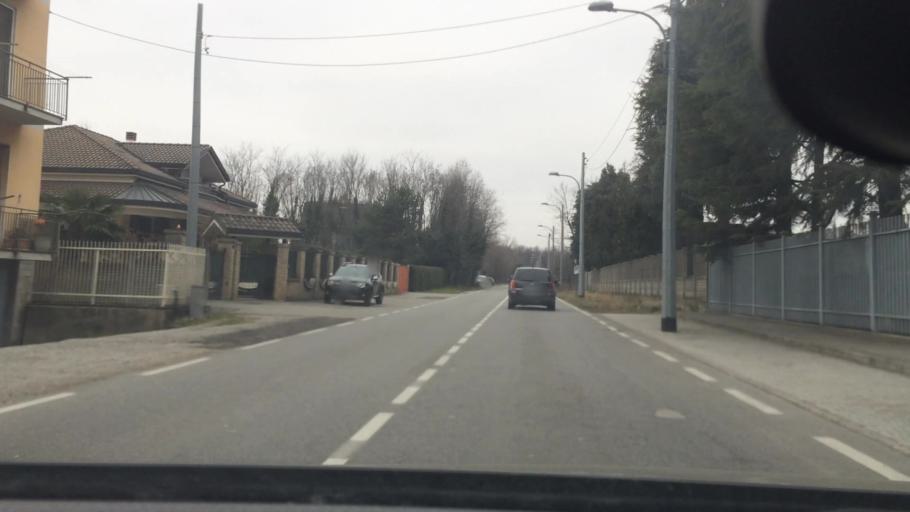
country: IT
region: Lombardy
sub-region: Provincia di Monza e Brianza
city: Cogliate
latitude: 45.6408
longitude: 9.1046
